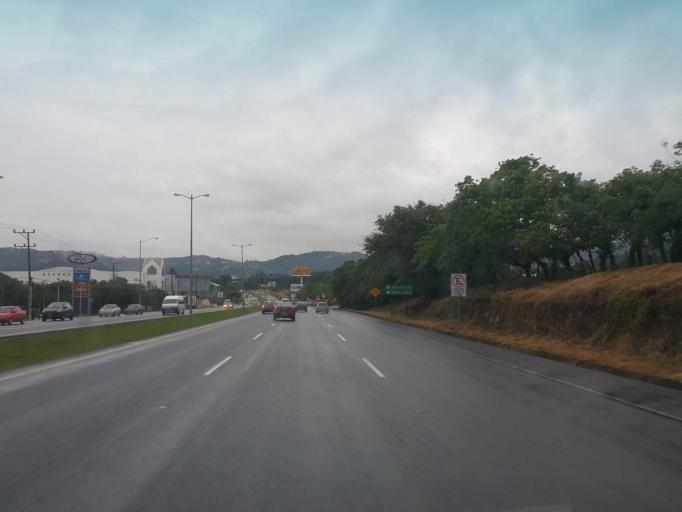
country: CR
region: San Jose
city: Santa Ana
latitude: 9.9368
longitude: -84.2160
